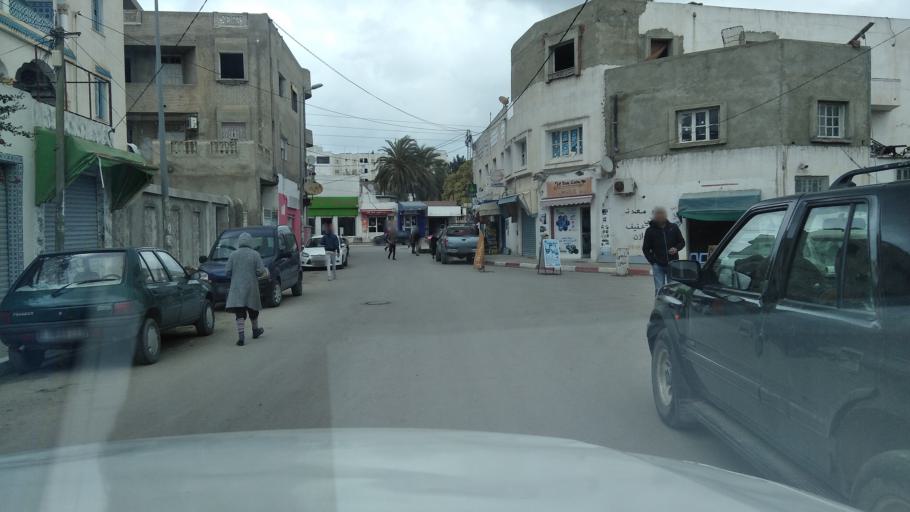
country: TN
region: Bin 'Arus
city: Ben Arous
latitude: 36.7407
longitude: 10.2373
